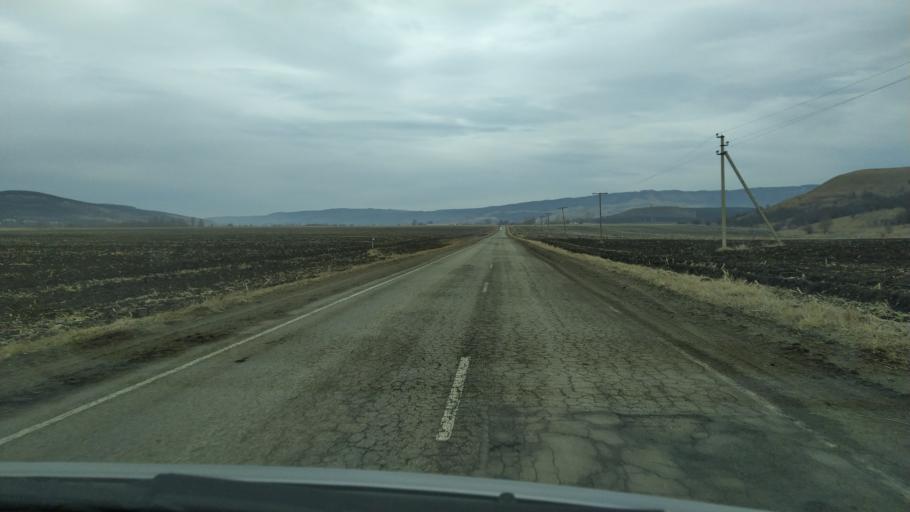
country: RU
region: Krasnodarskiy
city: Peredovaya
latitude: 44.1083
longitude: 41.4327
